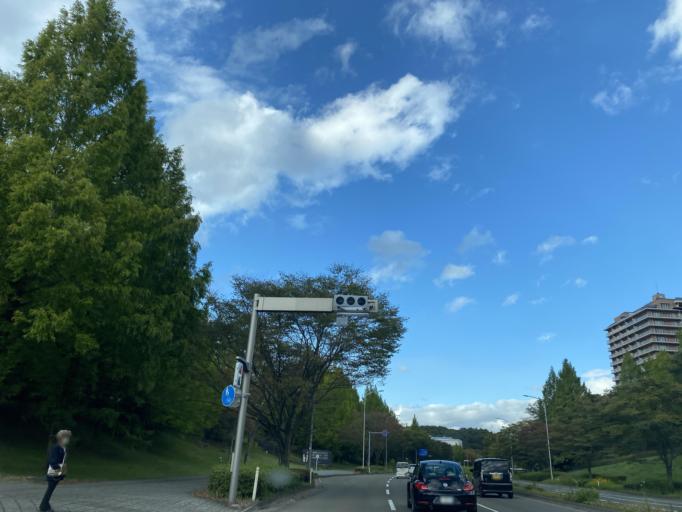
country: JP
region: Miyagi
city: Tomiya
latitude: 38.3405
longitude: 140.8386
